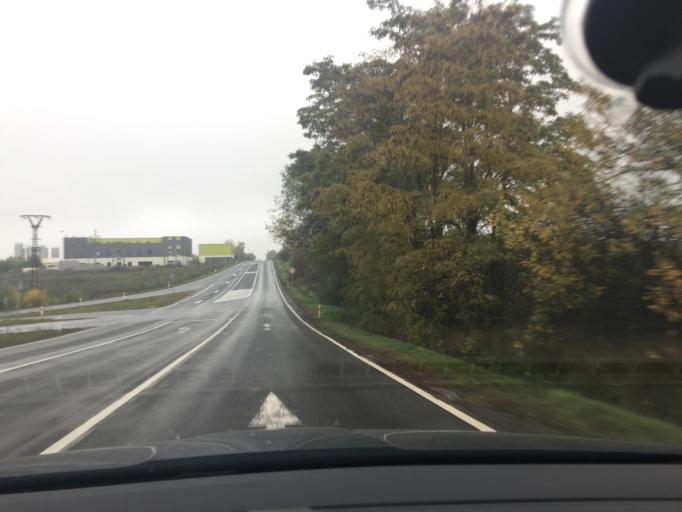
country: CZ
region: South Moravian
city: Blazovice
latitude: 49.1843
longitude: 16.8088
